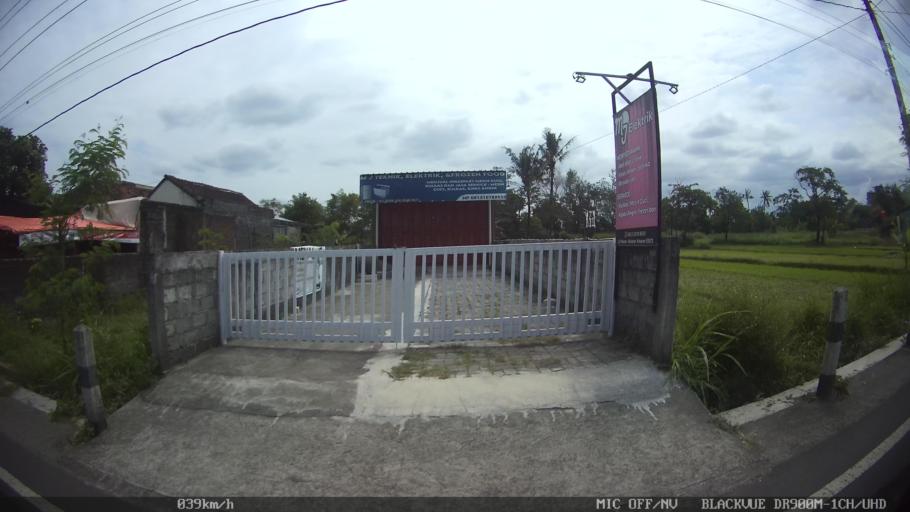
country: ID
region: Central Java
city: Candi Prambanan
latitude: -7.7401
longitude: 110.4816
